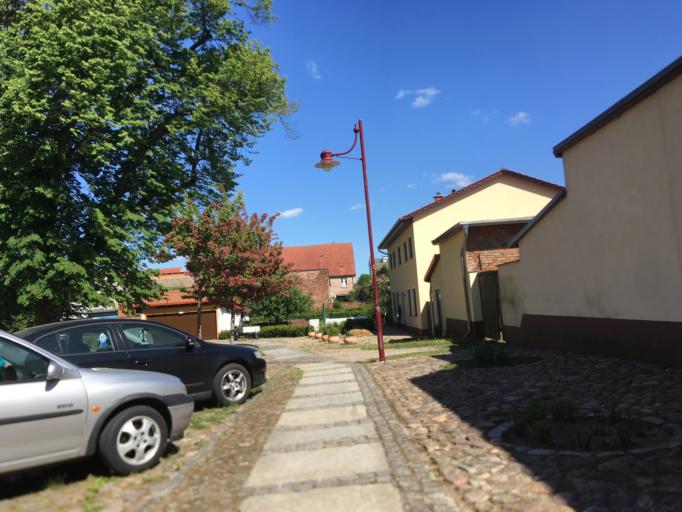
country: DE
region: Brandenburg
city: Joachimsthal
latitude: 52.9775
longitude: 13.7422
